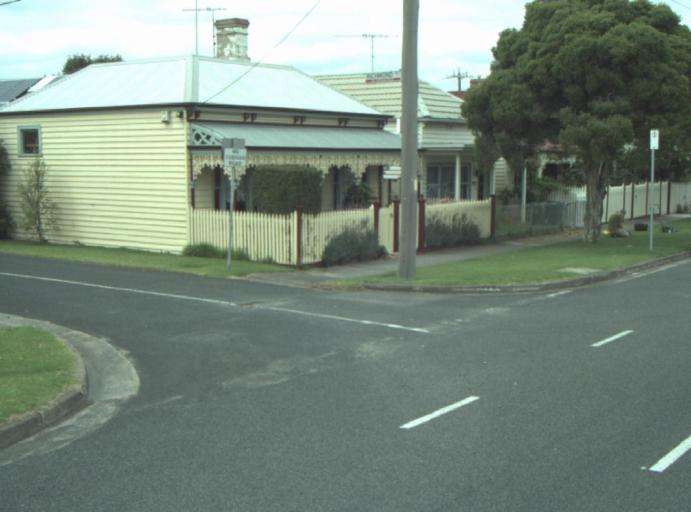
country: AU
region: Victoria
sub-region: Greater Geelong
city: East Geelong
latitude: -38.1601
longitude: 144.3634
